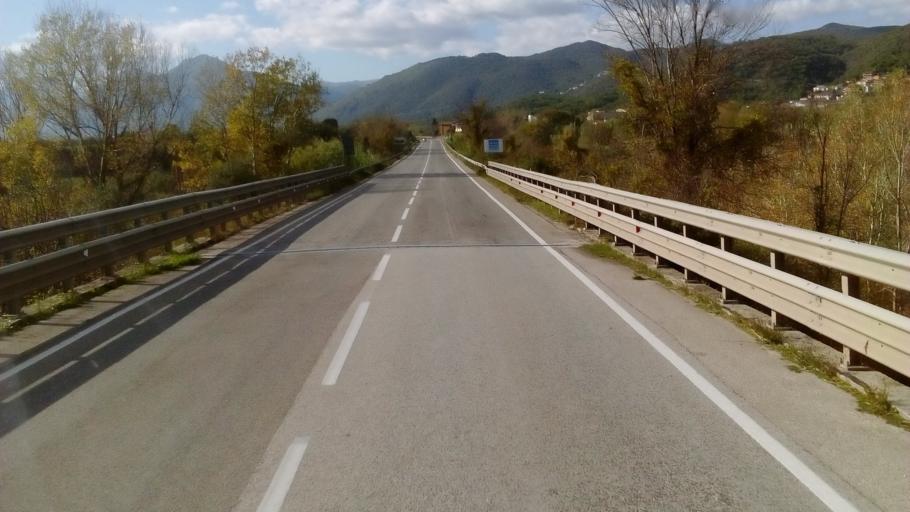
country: IT
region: Molise
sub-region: Provincia di Isernia
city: Taverna Ravindola
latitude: 41.5181
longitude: 14.1350
